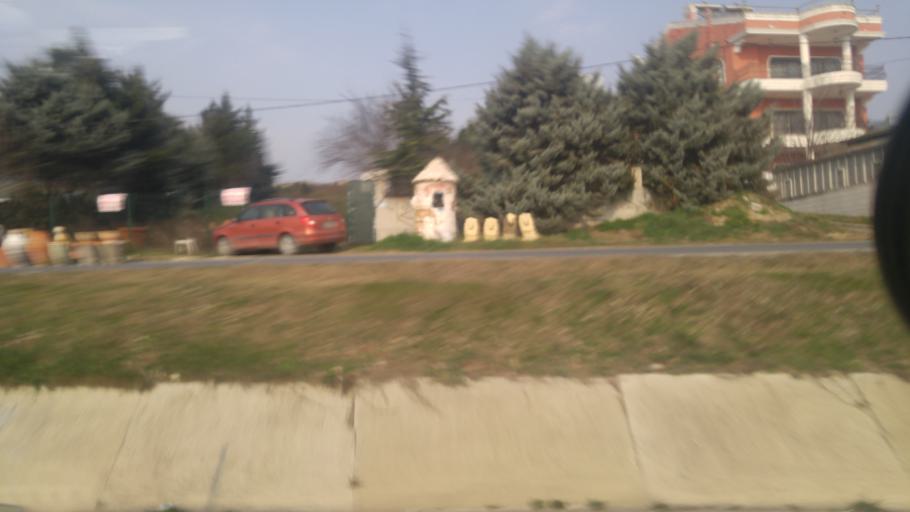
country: TR
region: Istanbul
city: Kumburgaz
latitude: 41.0134
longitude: 28.4943
